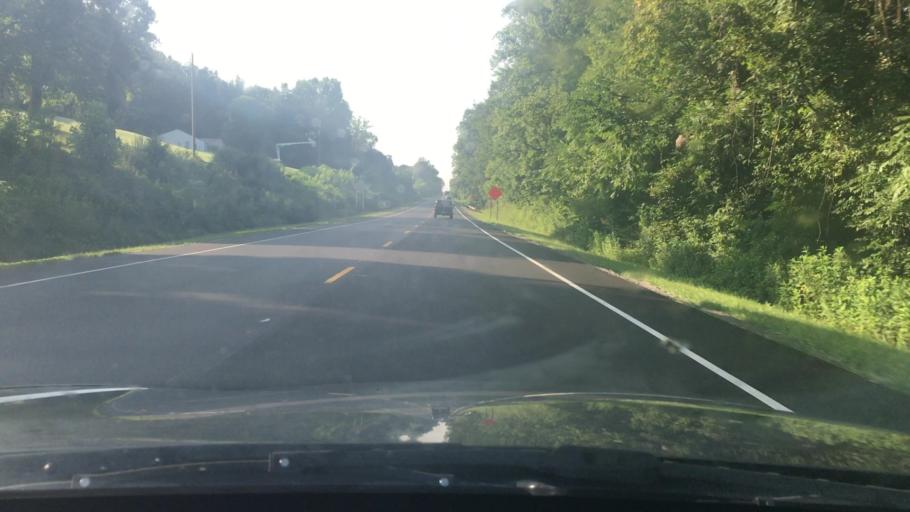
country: US
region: North Carolina
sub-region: Caswell County
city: Yanceyville
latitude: 36.4622
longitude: -79.3727
